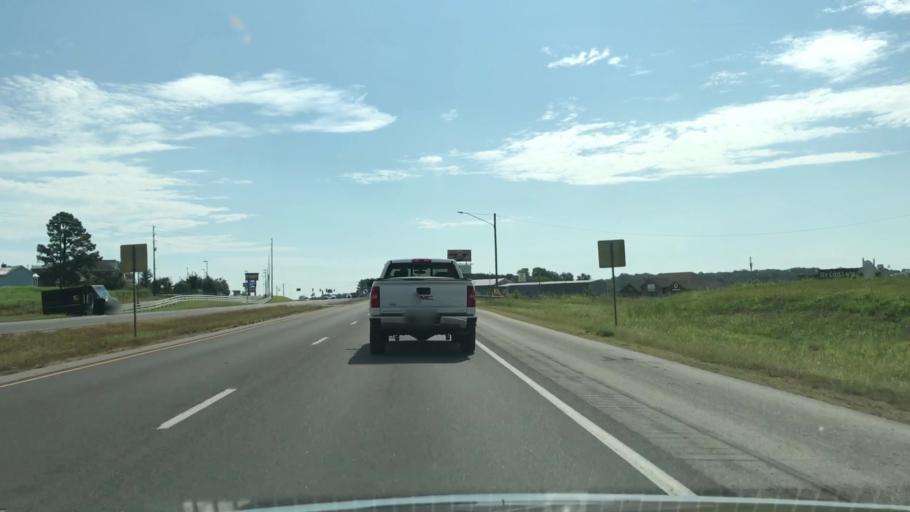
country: US
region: Kentucky
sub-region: Allen County
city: Scottsville
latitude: 36.7570
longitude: -86.2223
